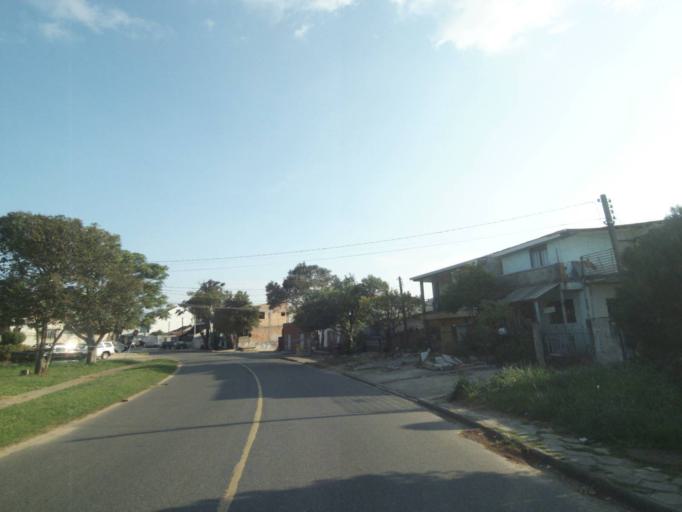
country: BR
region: Parana
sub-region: Curitiba
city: Curitiba
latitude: -25.4849
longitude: -49.3364
